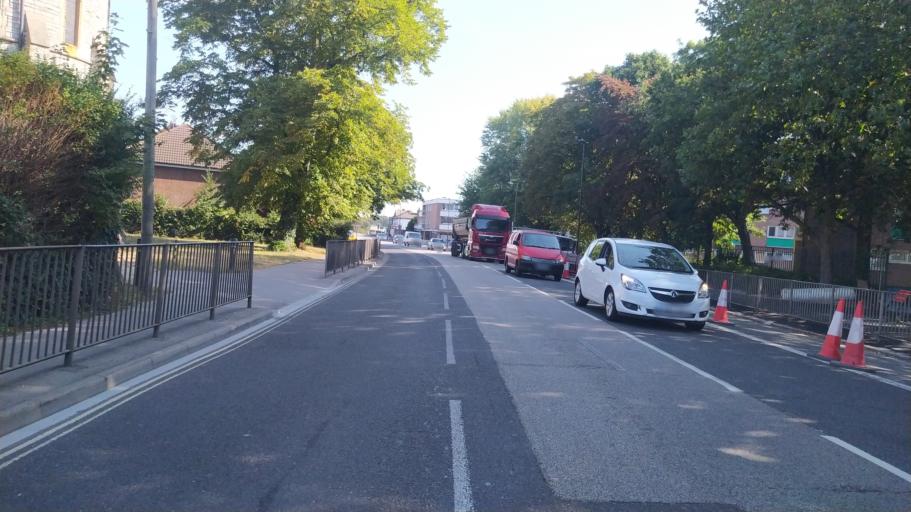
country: GB
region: England
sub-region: Southampton
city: Southampton
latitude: 50.9105
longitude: -1.3889
